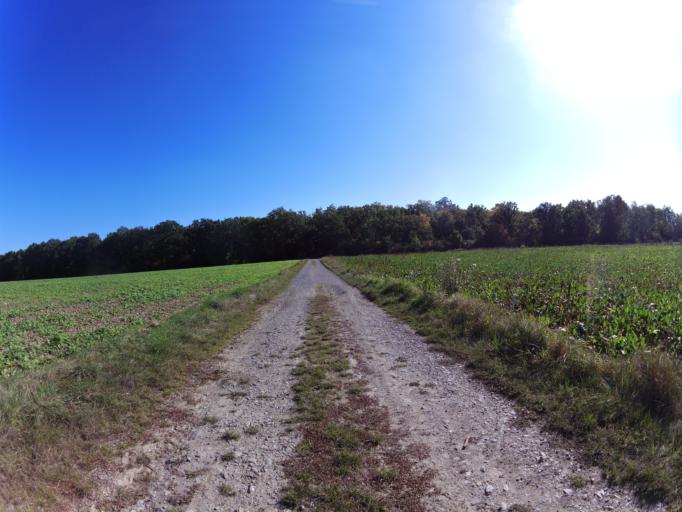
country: DE
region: Bavaria
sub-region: Regierungsbezirk Unterfranken
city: Sommerhausen
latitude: 49.6838
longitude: 10.0407
